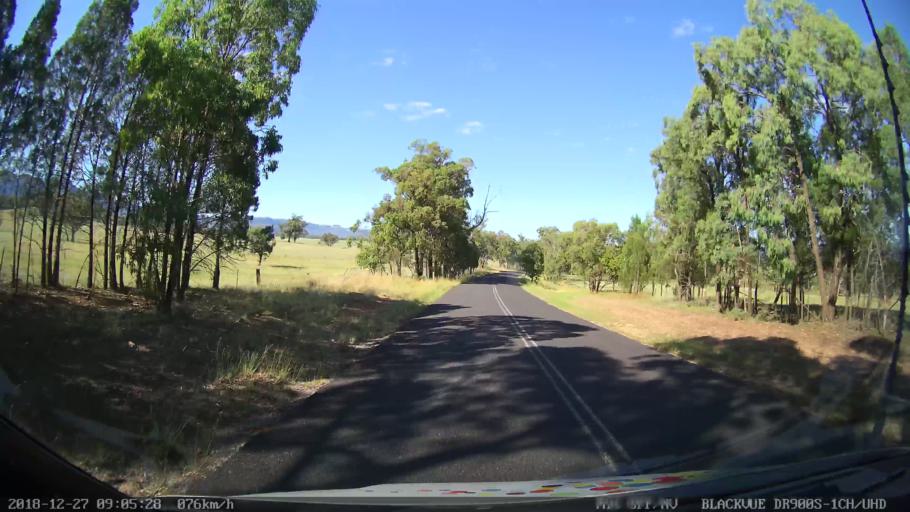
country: AU
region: New South Wales
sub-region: Lithgow
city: Portland
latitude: -33.1177
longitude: 150.1798
